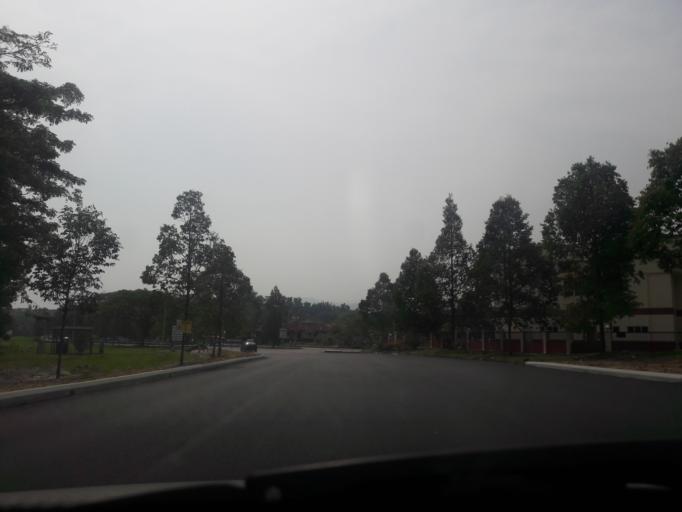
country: MY
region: Kedah
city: Kulim
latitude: 5.3682
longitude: 100.5601
